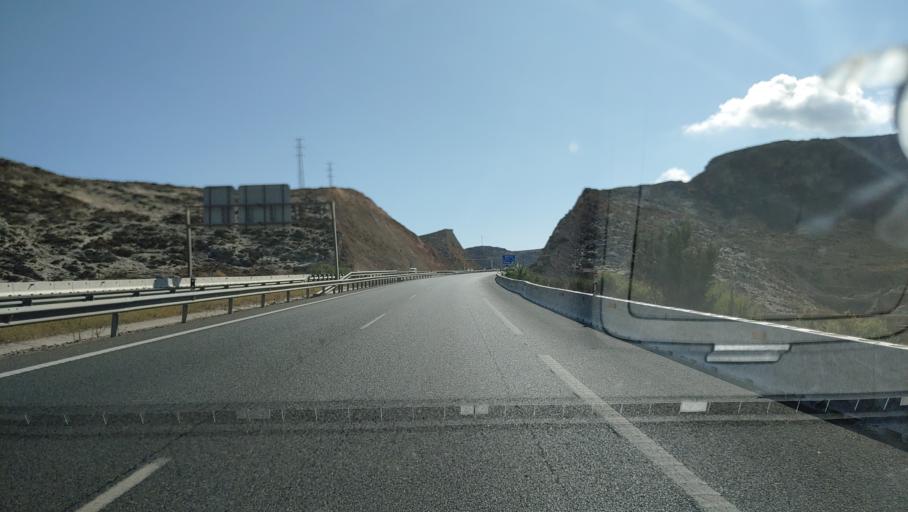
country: ES
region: Andalusia
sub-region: Provincia de Almeria
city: Almeria
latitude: 36.8500
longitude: -2.4756
